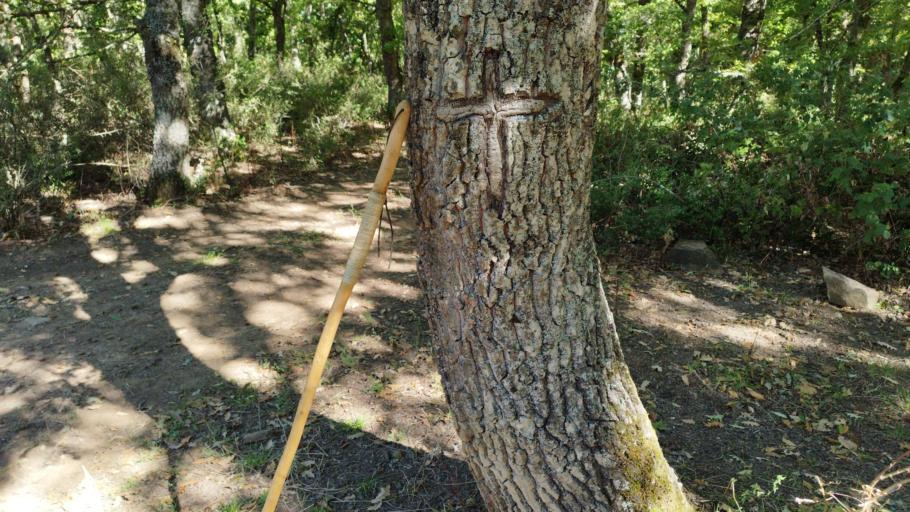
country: IT
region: Sicily
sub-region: Messina
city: Castel di Lucio
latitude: 37.8480
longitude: 14.3570
